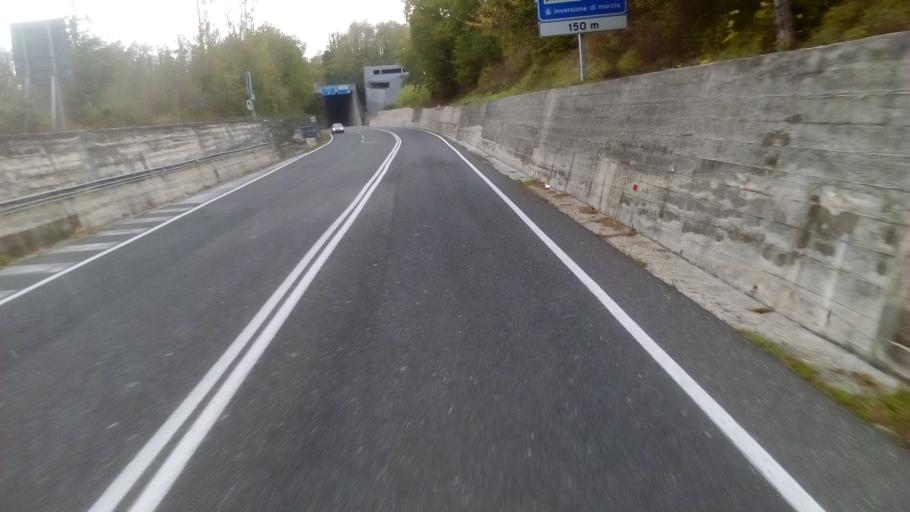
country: IT
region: Molise
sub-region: Provincia di Isernia
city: Isernia
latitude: 41.5917
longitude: 14.2439
